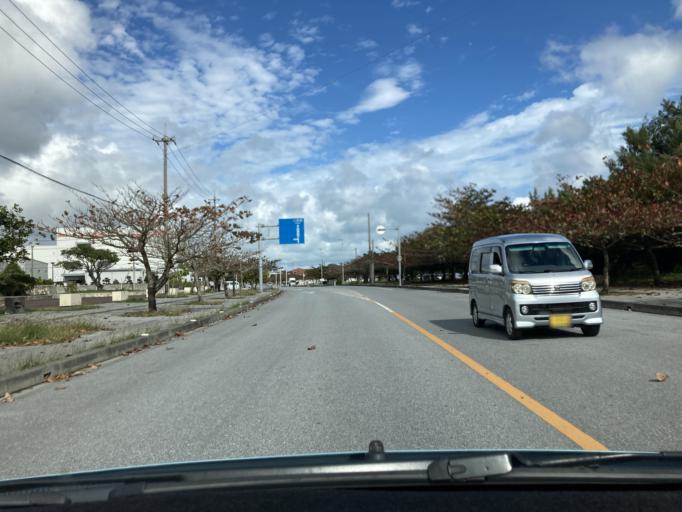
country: JP
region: Okinawa
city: Ginowan
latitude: 26.2159
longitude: 127.7750
